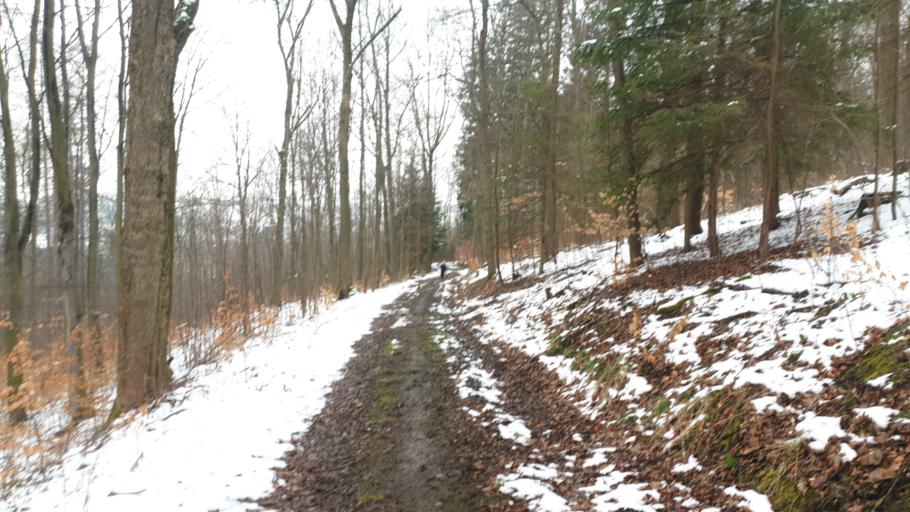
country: DE
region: Saxony
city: Gornau
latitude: 50.7703
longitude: 12.9884
